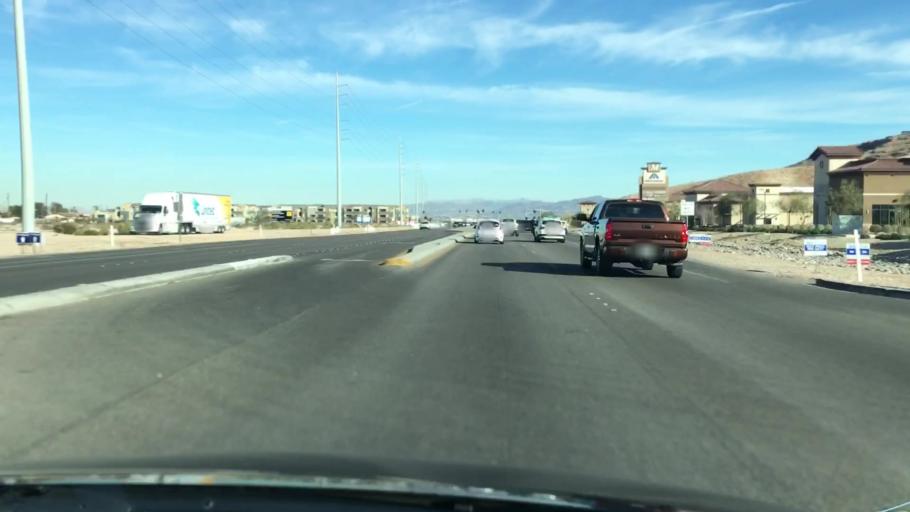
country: US
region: Nevada
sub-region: Clark County
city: Enterprise
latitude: 36.0201
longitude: -115.2656
